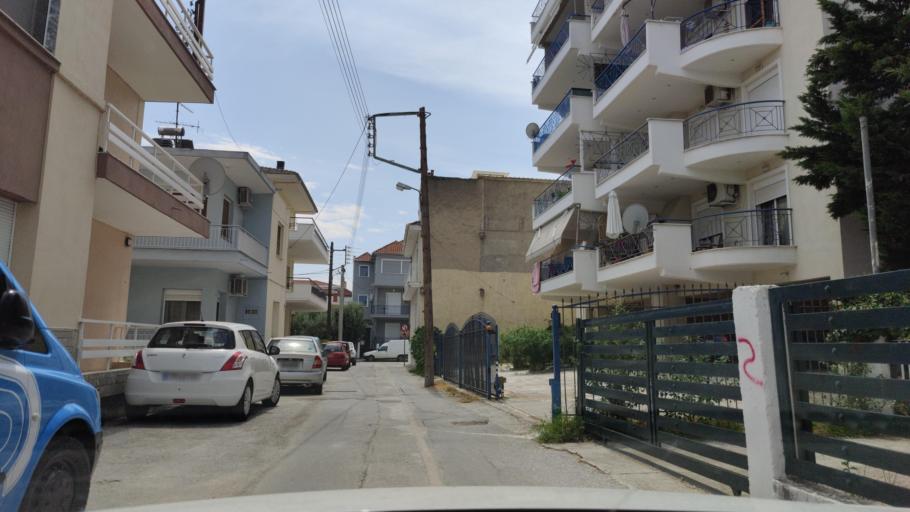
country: GR
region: Central Macedonia
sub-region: Nomos Serron
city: Serres
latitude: 41.0815
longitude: 23.5429
